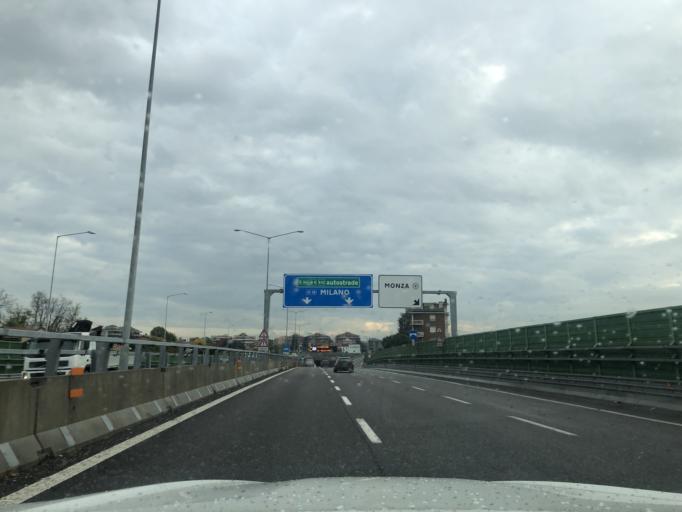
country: IT
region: Lombardy
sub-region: Provincia di Monza e Brianza
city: Muggio
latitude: 45.5876
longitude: 9.2486
